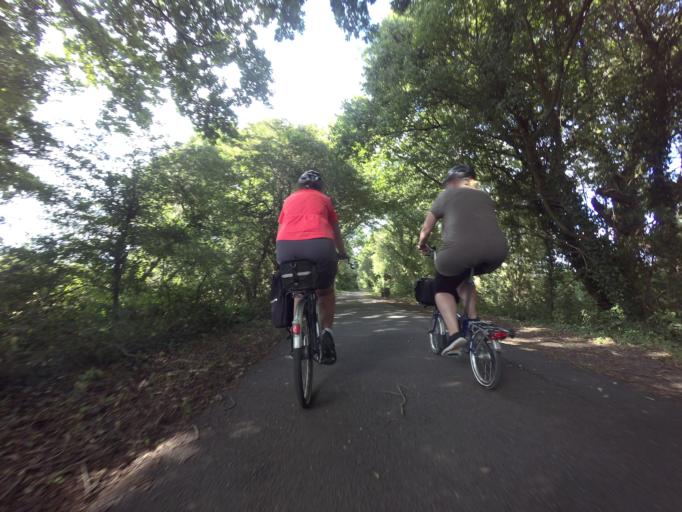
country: GB
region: England
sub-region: East Sussex
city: Hailsham
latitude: 50.8481
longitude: 0.2561
